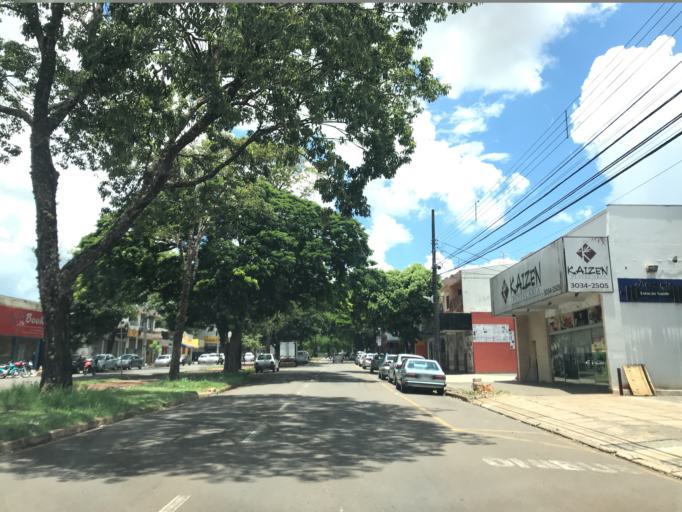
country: BR
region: Parana
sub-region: Maringa
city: Maringa
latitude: -23.3994
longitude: -51.9198
